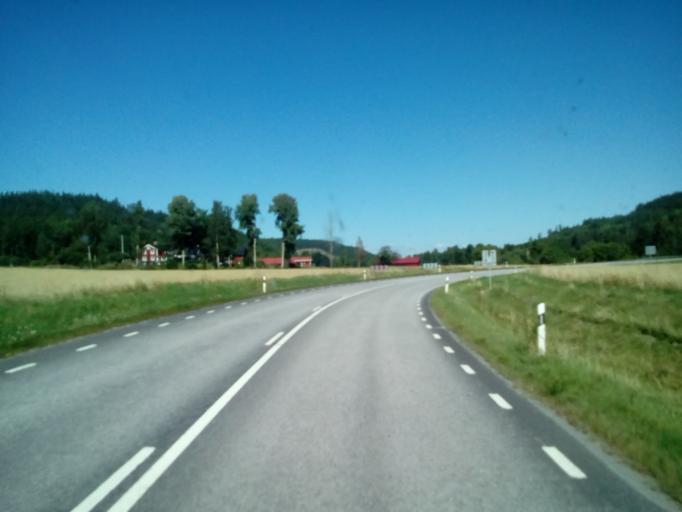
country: SE
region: OEstergoetland
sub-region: Kinda Kommun
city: Kisa
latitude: 58.0179
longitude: 15.6488
